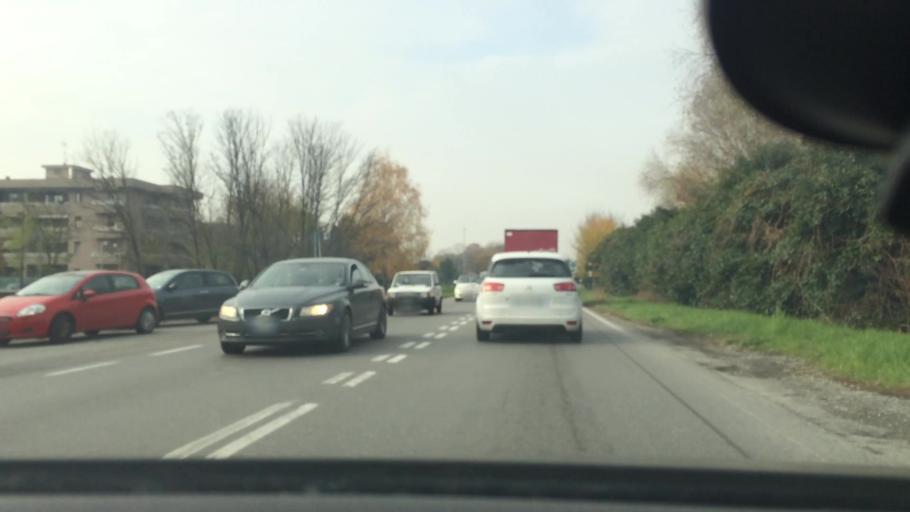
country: IT
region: Lombardy
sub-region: Provincia di Monza e Brianza
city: Bovisio-Masciago
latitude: 45.6041
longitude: 9.1529
